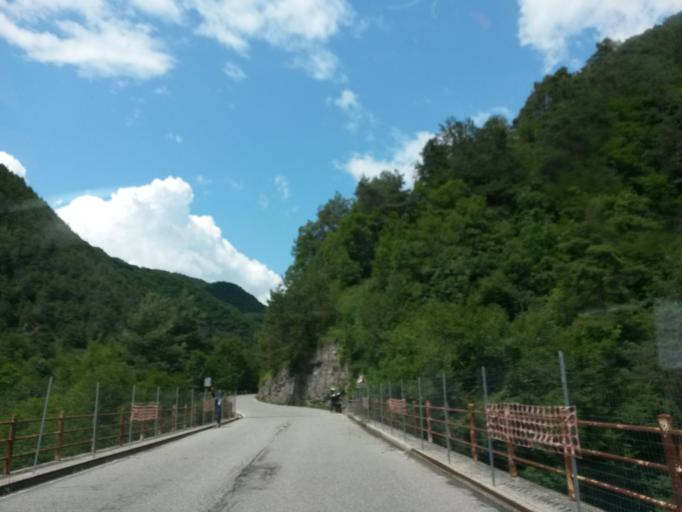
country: IT
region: Lombardy
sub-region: Provincia di Brescia
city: Valvestino
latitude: 45.7363
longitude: 10.6053
